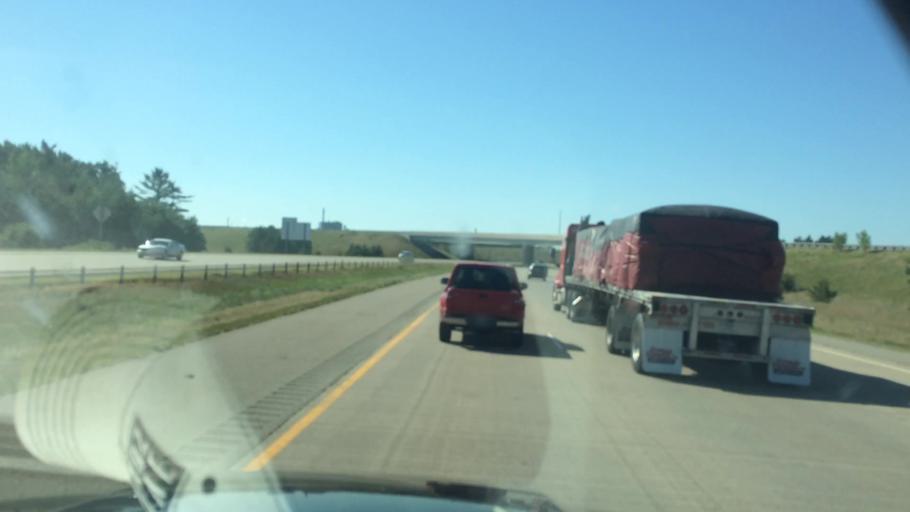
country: US
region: Wisconsin
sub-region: Marathon County
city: Rothschild
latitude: 44.8992
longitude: -89.6420
